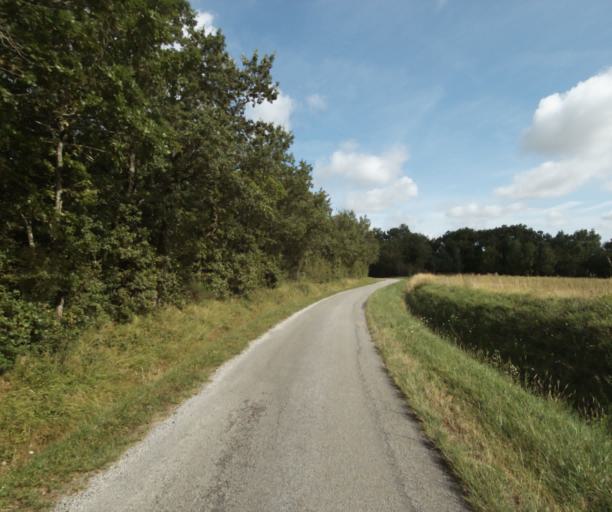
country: FR
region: Midi-Pyrenees
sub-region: Departement du Tarn
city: Soreze
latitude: 43.4691
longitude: 2.0841
